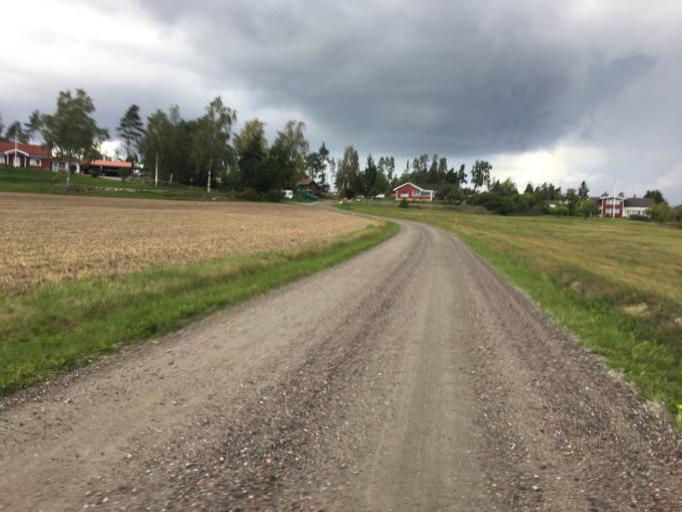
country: SE
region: Soedermanland
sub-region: Eskilstuna Kommun
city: Arla
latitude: 59.4516
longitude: 16.6673
